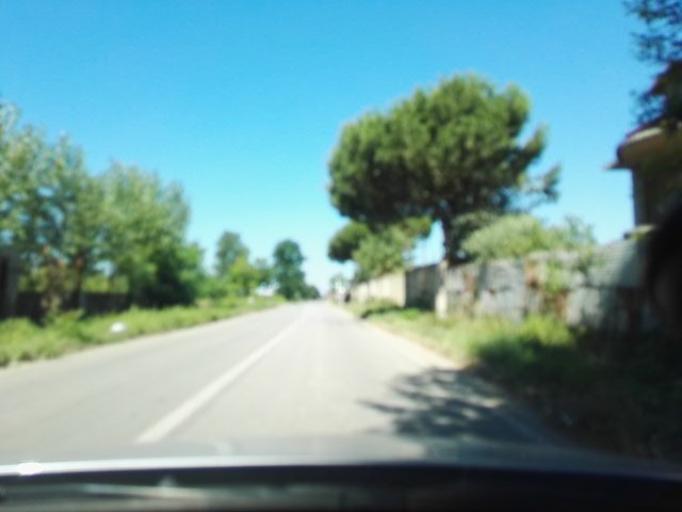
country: IT
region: Campania
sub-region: Provincia di Caserta
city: Casapesenna
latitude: 40.9853
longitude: 14.1401
